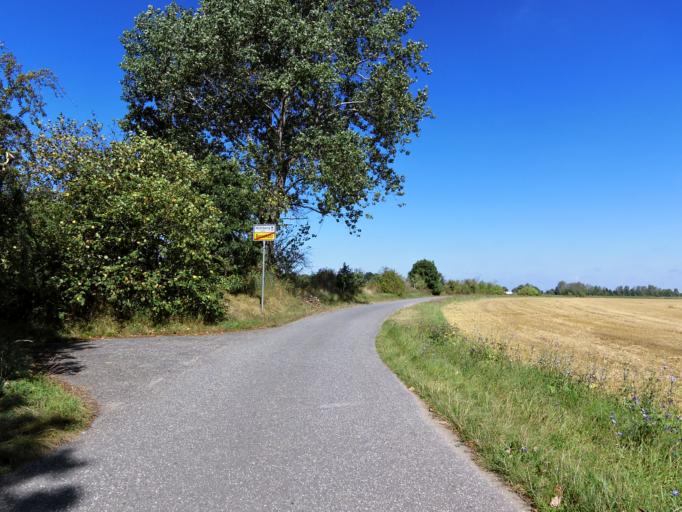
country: DE
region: Brandenburg
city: Muhlberg
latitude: 51.4097
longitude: 13.2169
